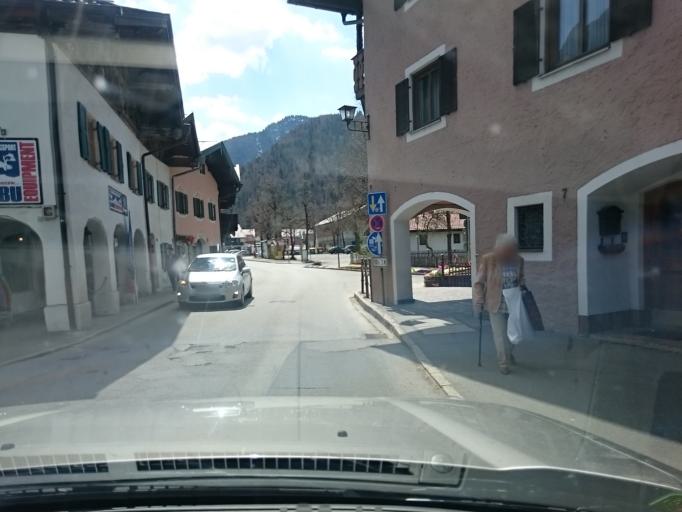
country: DE
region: Bavaria
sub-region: Upper Bavaria
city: Mittenwald
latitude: 47.4394
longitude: 11.2609
